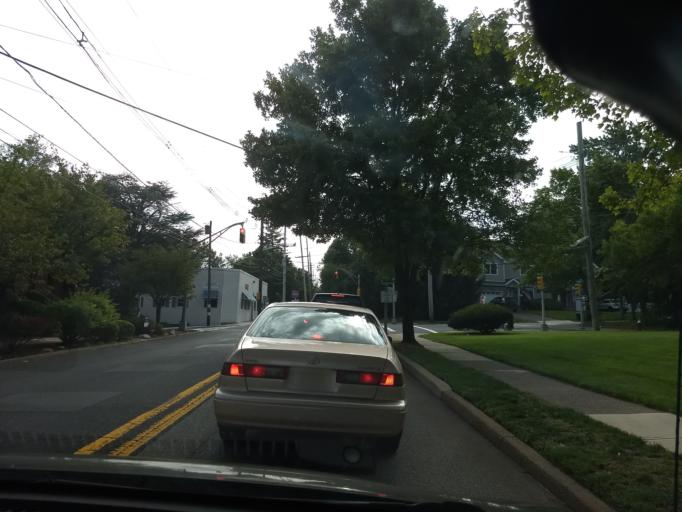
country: US
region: New Jersey
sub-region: Bergen County
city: Ridgewood
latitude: 40.9753
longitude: -74.1153
